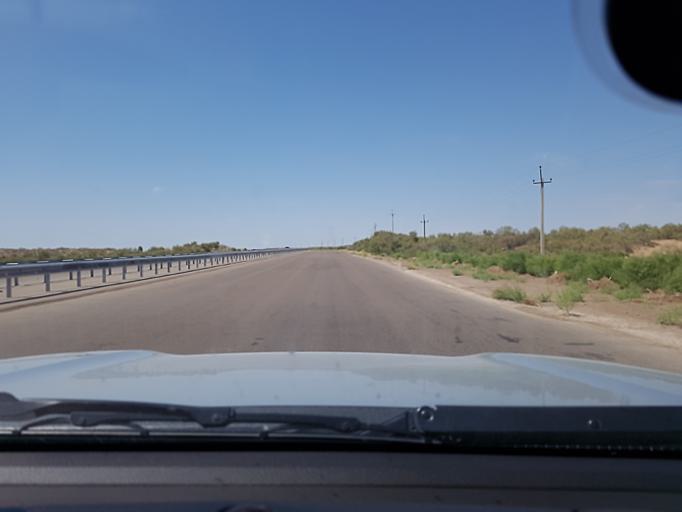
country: TM
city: Akdepe
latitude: 41.7515
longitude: 59.2975
